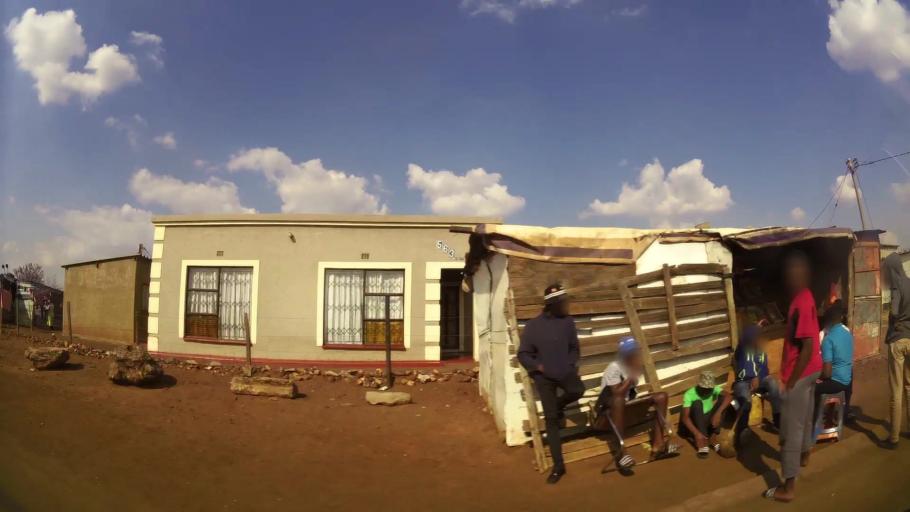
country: ZA
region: Gauteng
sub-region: Ekurhuleni Metropolitan Municipality
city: Germiston
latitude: -26.3382
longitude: 28.1365
